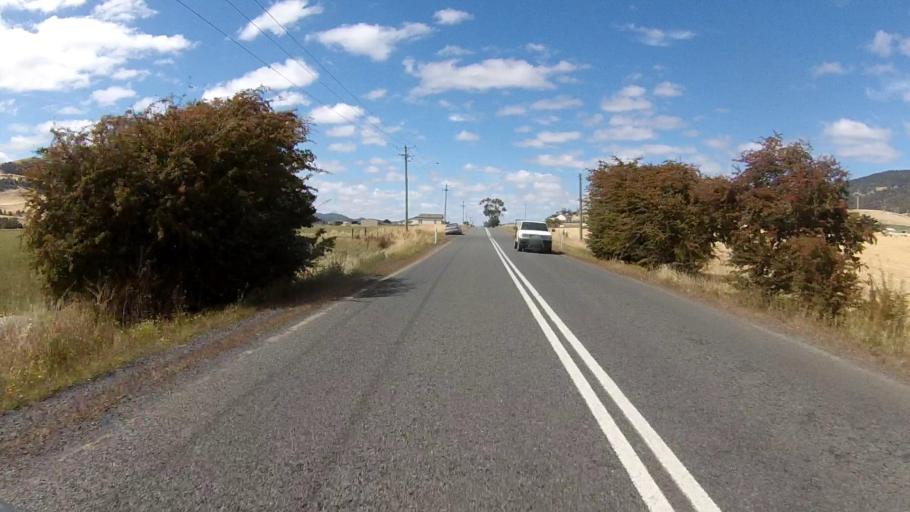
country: AU
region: Tasmania
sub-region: Brighton
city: Bridgewater
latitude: -42.5889
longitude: 147.4090
